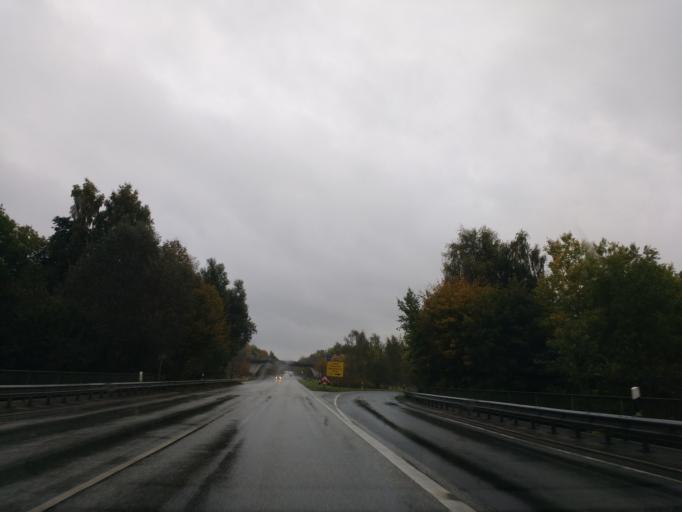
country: DE
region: Schleswig-Holstein
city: Susel
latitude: 54.0824
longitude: 10.6943
